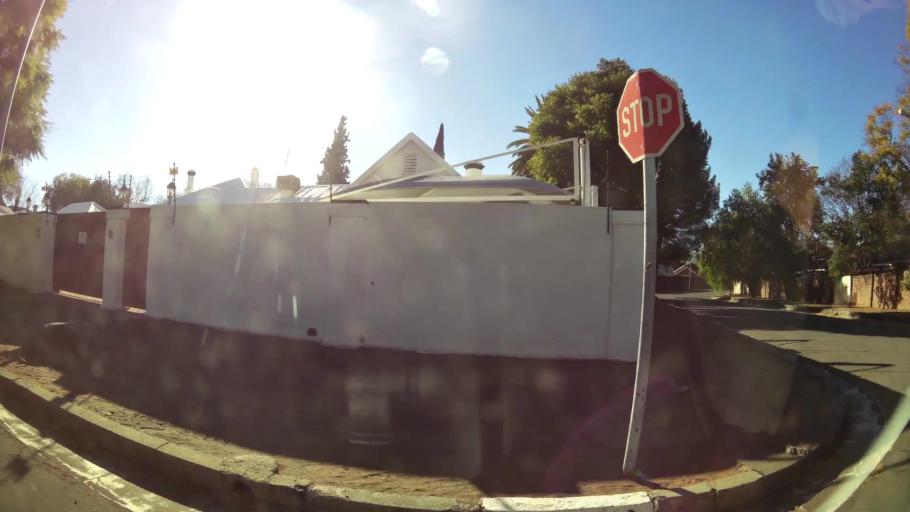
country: ZA
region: Northern Cape
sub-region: Frances Baard District Municipality
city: Kimberley
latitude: -28.7458
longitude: 24.7766
